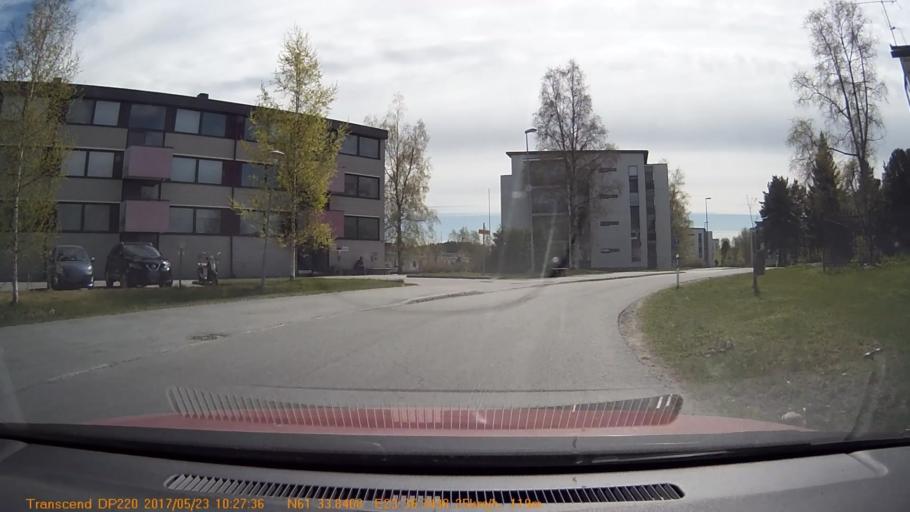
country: FI
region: Pirkanmaa
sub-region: Tampere
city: Yloejaervi
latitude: 61.5643
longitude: 23.6056
